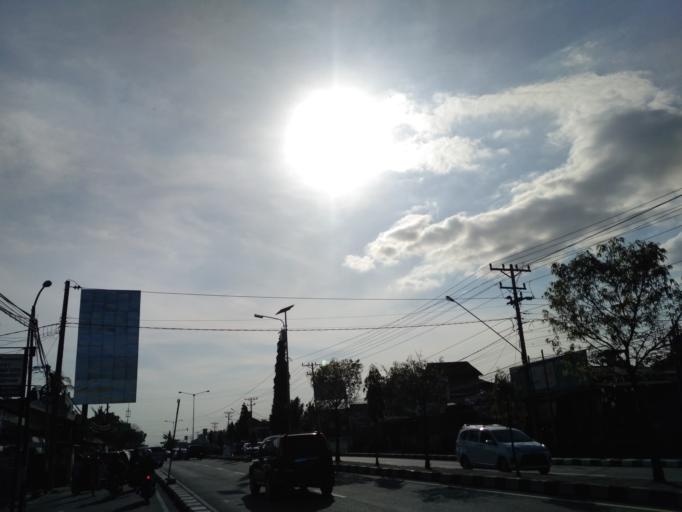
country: ID
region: Daerah Istimewa Yogyakarta
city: Depok
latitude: -7.7650
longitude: 110.4257
